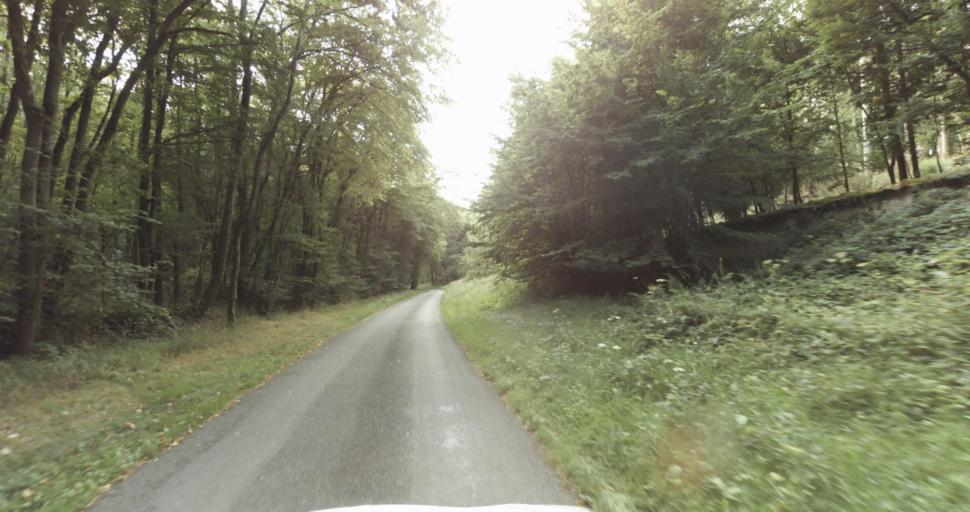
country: FR
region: Haute-Normandie
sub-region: Departement de l'Eure
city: Tillieres-sur-Avre
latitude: 48.7728
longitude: 1.1075
